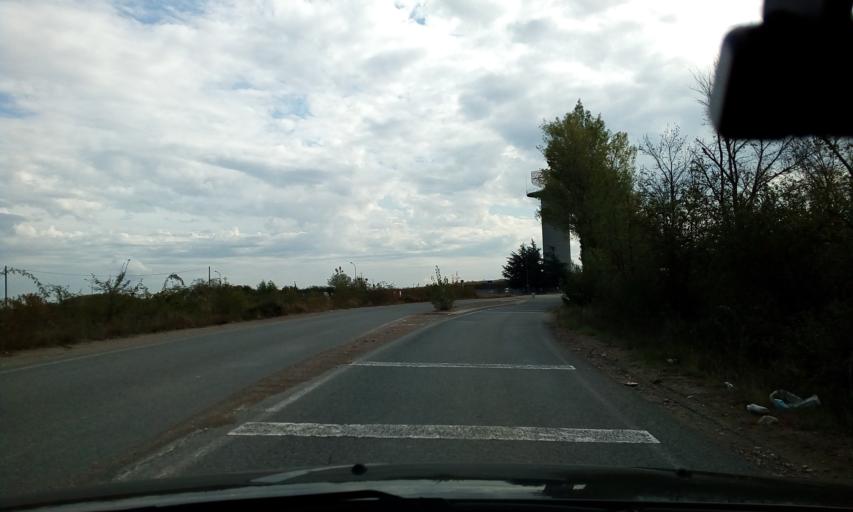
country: FR
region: Rhone-Alpes
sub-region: Departement du Rhone
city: Saint-Laurent-de-Mure
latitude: 45.6972
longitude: 5.0793
